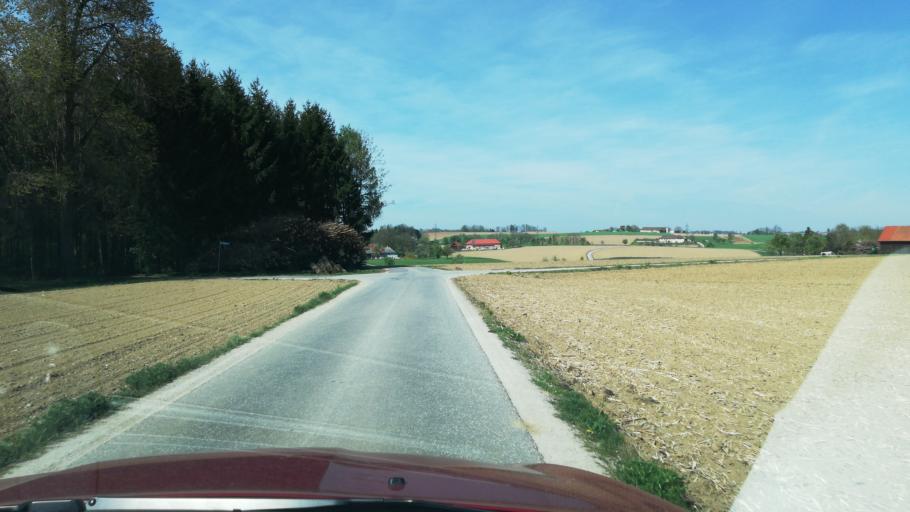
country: AT
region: Upper Austria
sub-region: Politischer Bezirk Steyr-Land
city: Pfarrkirchen bei Bad Hall
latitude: 48.0370
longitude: 14.1816
